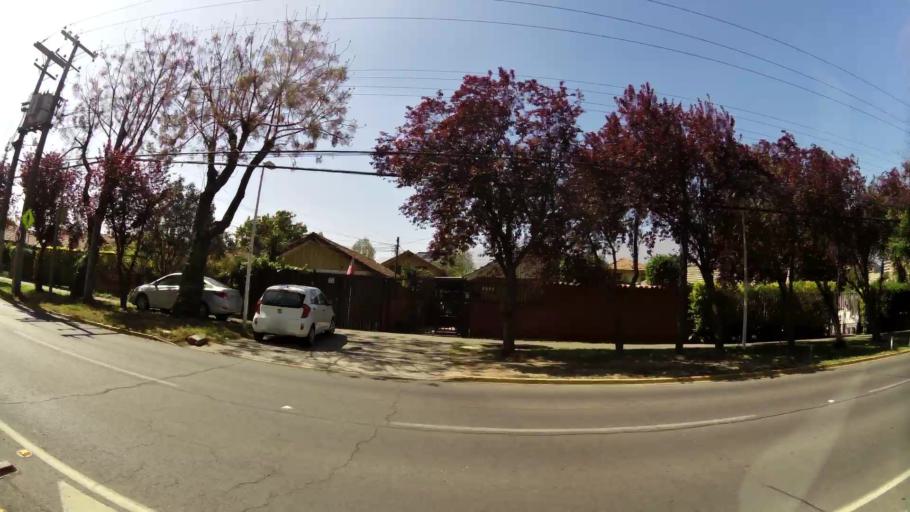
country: CL
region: Santiago Metropolitan
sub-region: Provincia de Santiago
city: Villa Presidente Frei, Nunoa, Santiago, Chile
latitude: -33.4263
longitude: -70.5521
